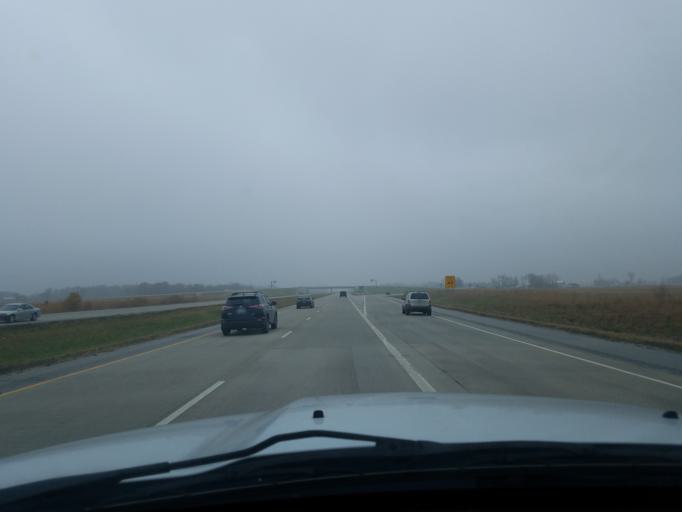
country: US
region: Indiana
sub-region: Howard County
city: Indian Heights
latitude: 40.4145
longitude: -86.0962
